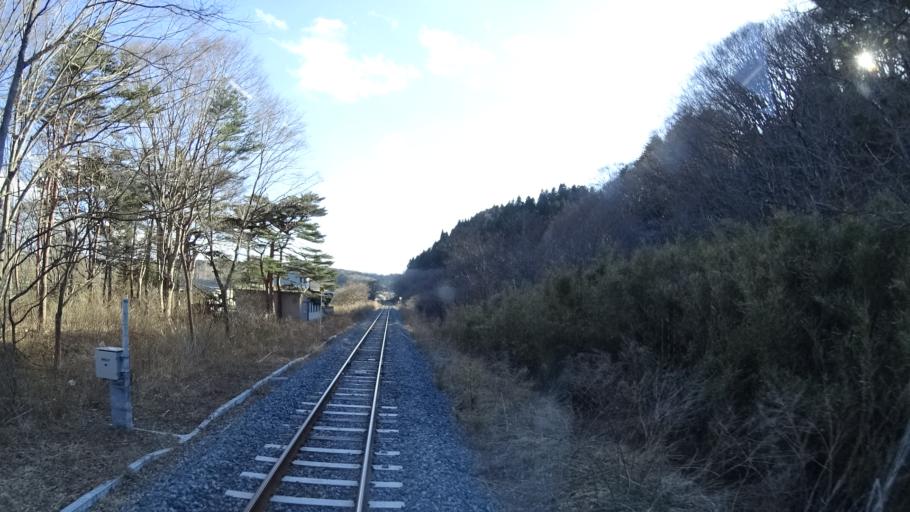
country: JP
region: Iwate
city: Miyako
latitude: 39.5712
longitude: 141.9326
